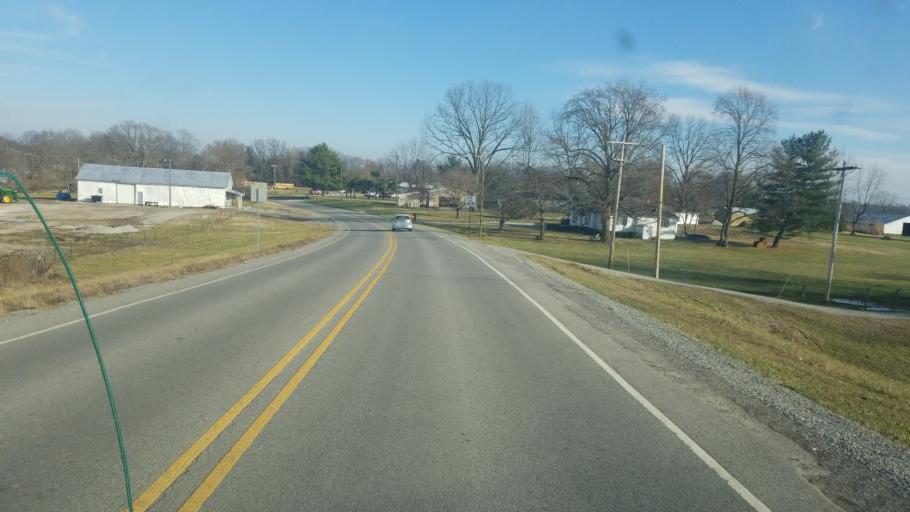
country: US
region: Illinois
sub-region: Wabash County
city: Mount Carmel
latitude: 38.4004
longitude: -87.7884
